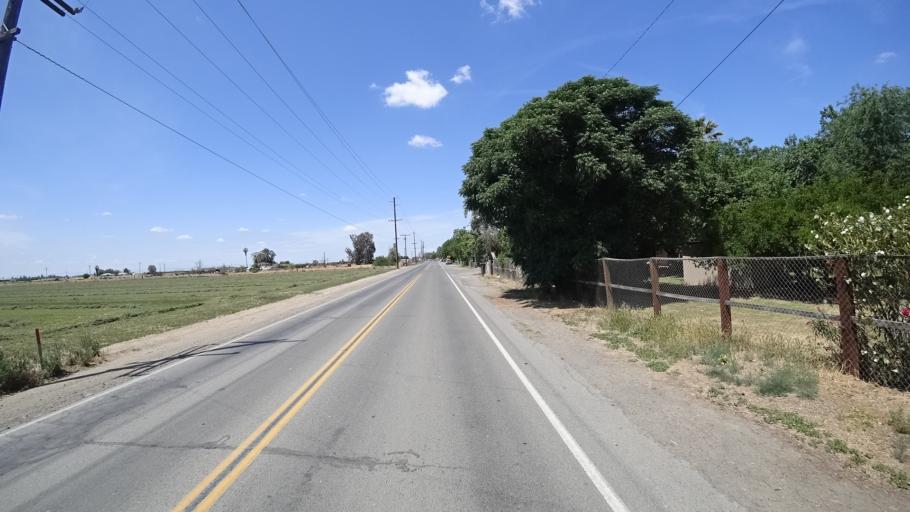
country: US
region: California
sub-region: Kings County
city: Home Garden
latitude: 36.2986
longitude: -119.6332
